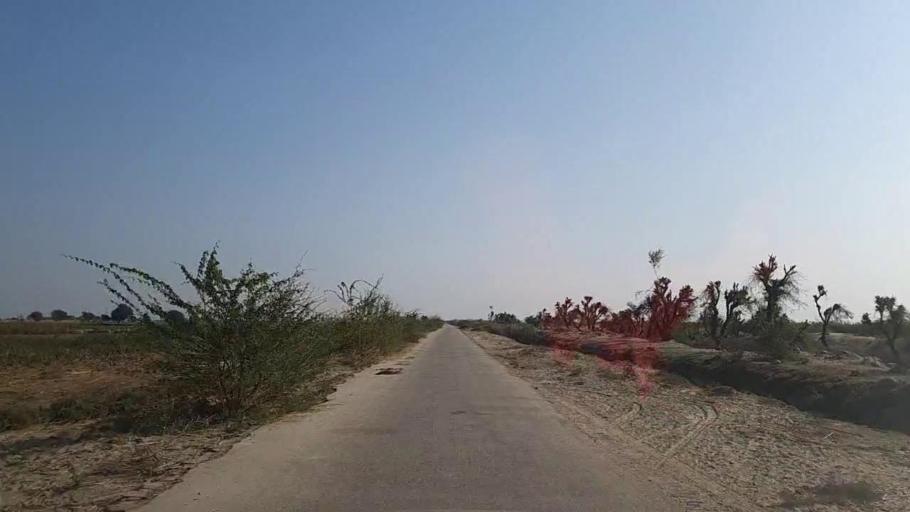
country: PK
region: Sindh
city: Sanghar
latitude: 25.9436
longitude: 69.0525
